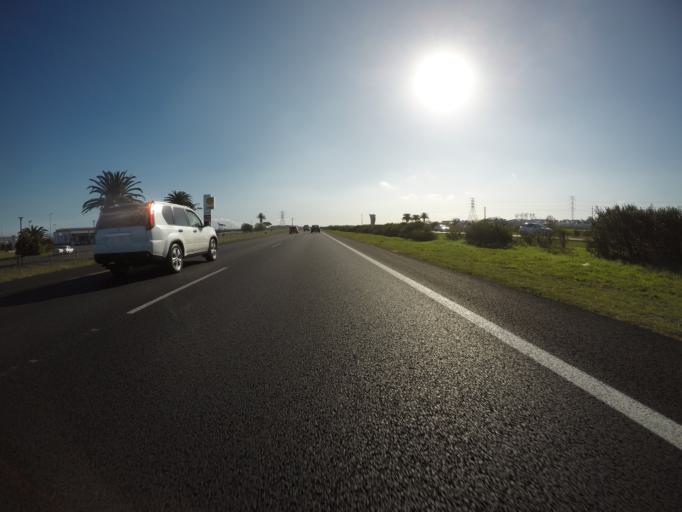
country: ZA
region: Western Cape
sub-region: Cape Winelands District Municipality
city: Stellenbosch
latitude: -34.0493
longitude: 18.7581
